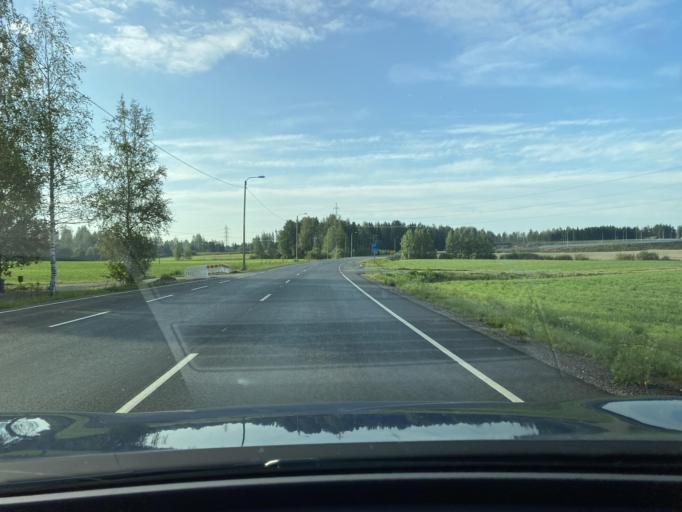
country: FI
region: Kymenlaakso
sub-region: Kouvola
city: Kouvola
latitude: 60.8781
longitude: 26.6025
